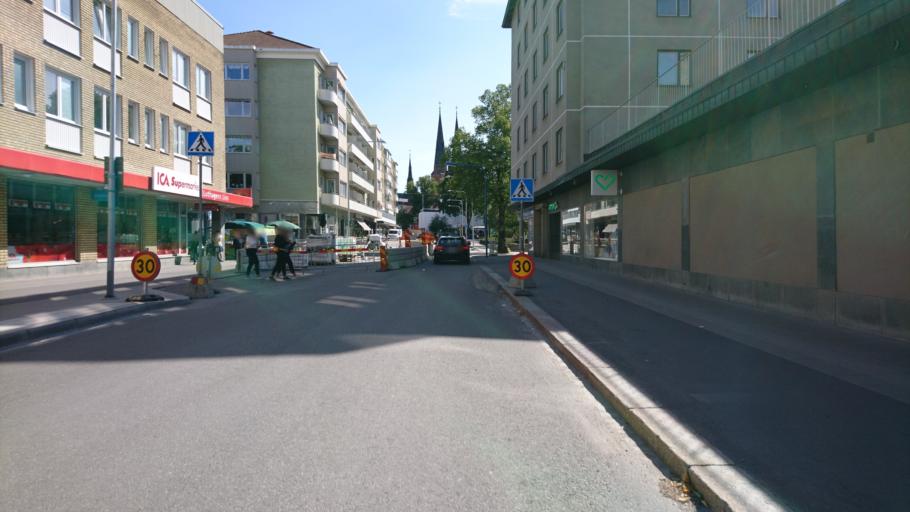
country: SE
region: Uppsala
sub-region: Uppsala Kommun
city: Uppsala
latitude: 59.8615
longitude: 17.6267
